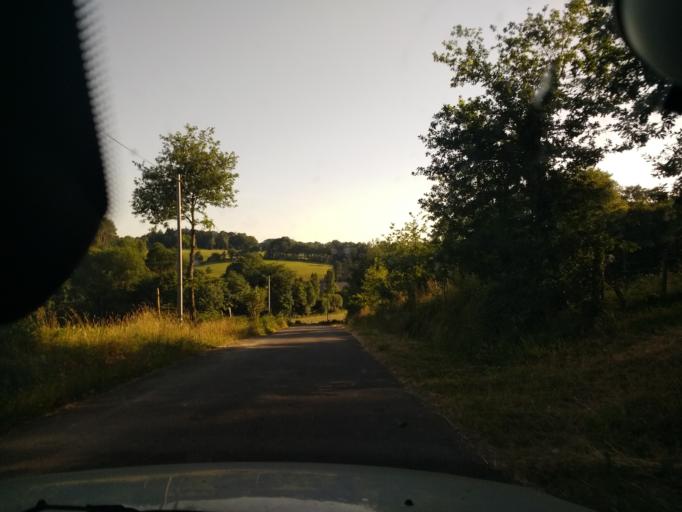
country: FR
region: Brittany
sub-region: Departement du Morbihan
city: Limerzel
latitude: 47.6294
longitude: -2.3549
